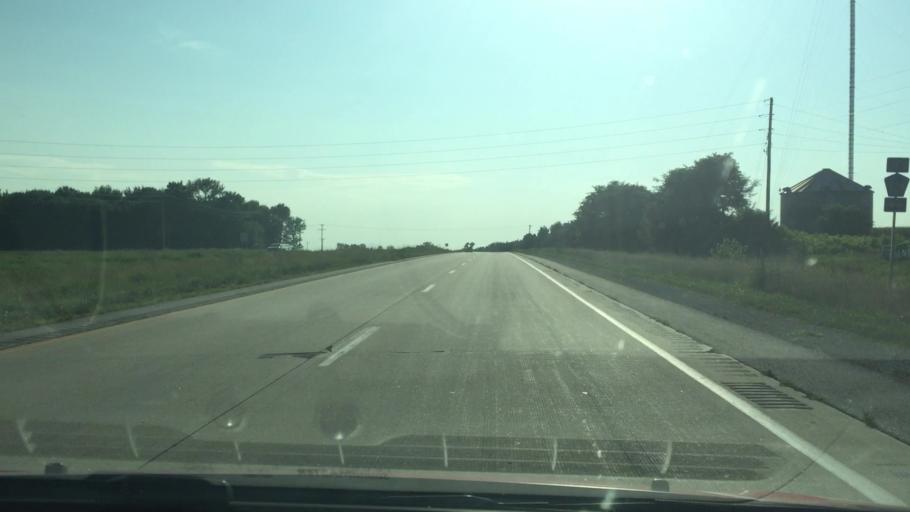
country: US
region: Iowa
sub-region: Cedar County
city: Durant
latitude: 41.5179
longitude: -90.8970
